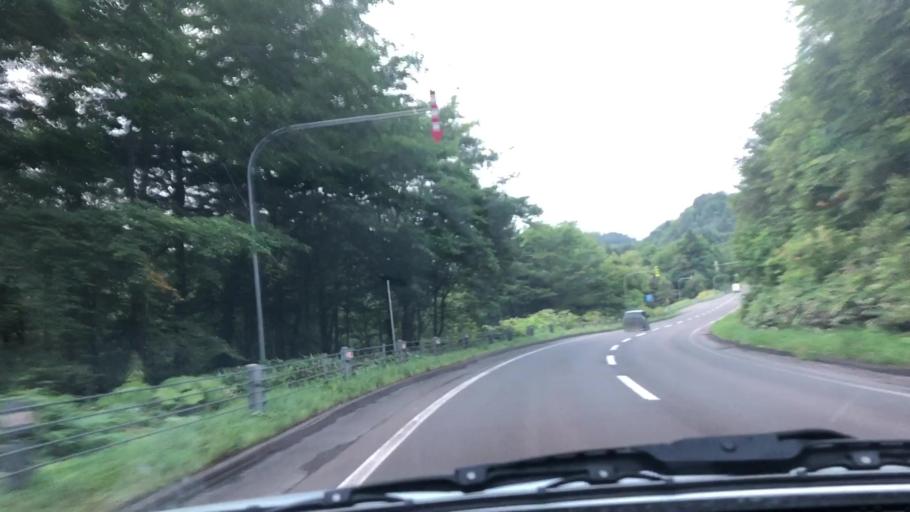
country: JP
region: Hokkaido
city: Iwamizawa
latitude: 42.8985
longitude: 142.1259
